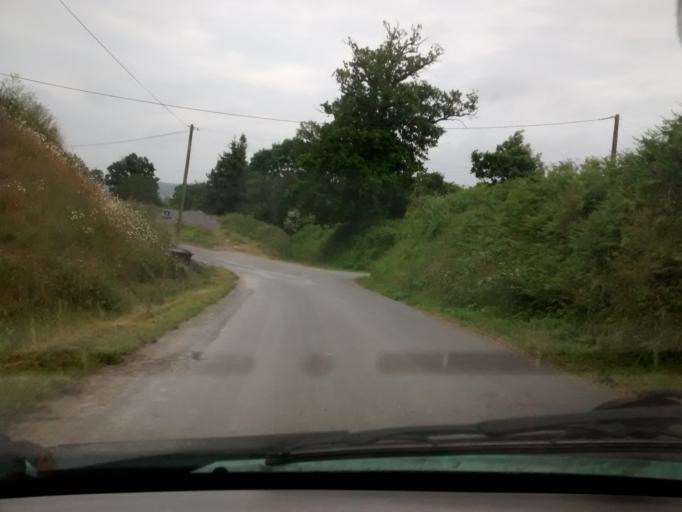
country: FR
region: Lower Normandy
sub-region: Departement de la Manche
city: Saint-Lo
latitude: 49.0978
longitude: -1.0651
